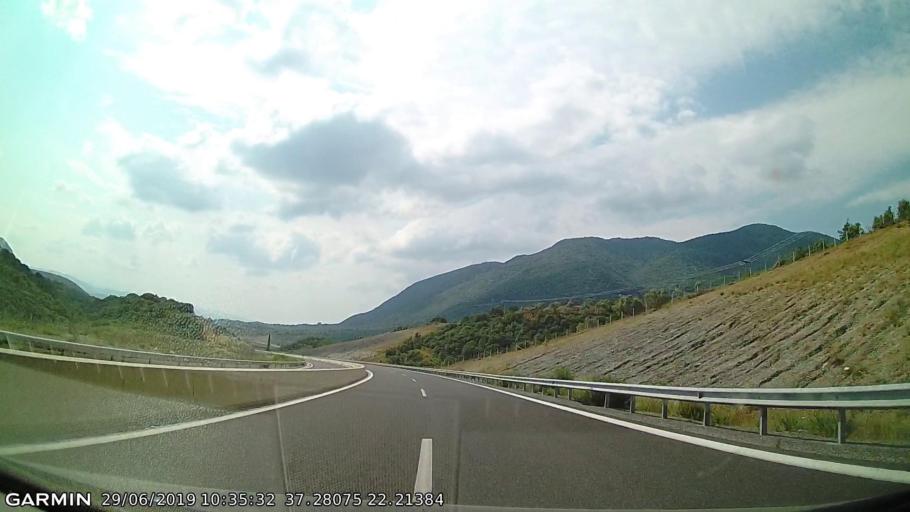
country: GR
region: Peloponnese
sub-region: Nomos Arkadias
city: Megalopoli
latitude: 37.2806
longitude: 22.2138
